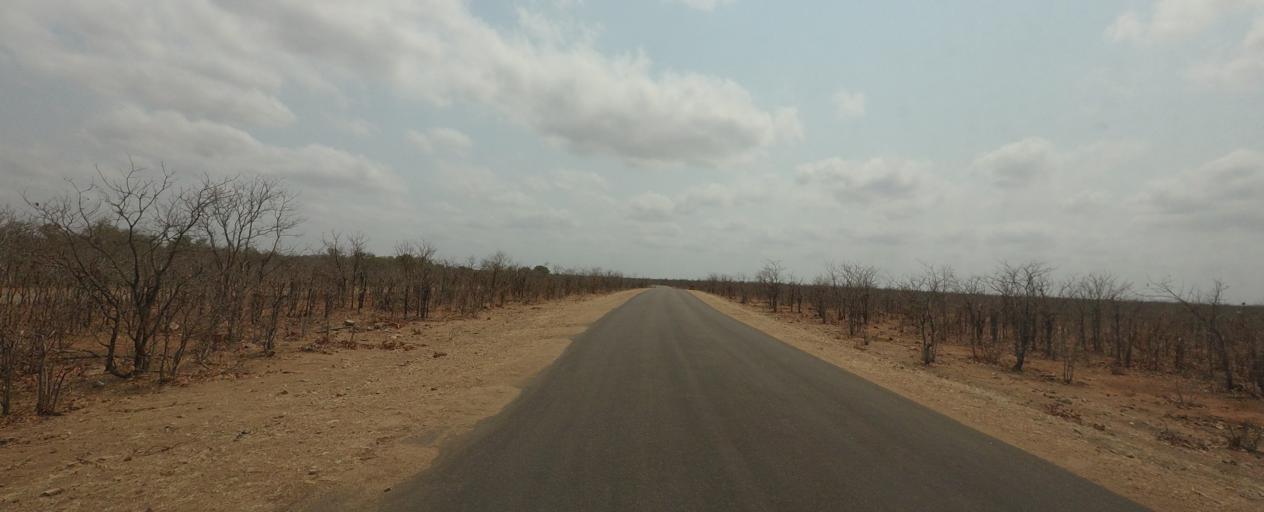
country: ZA
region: Limpopo
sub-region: Mopani District Municipality
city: Phalaborwa
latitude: -23.5471
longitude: 31.4285
